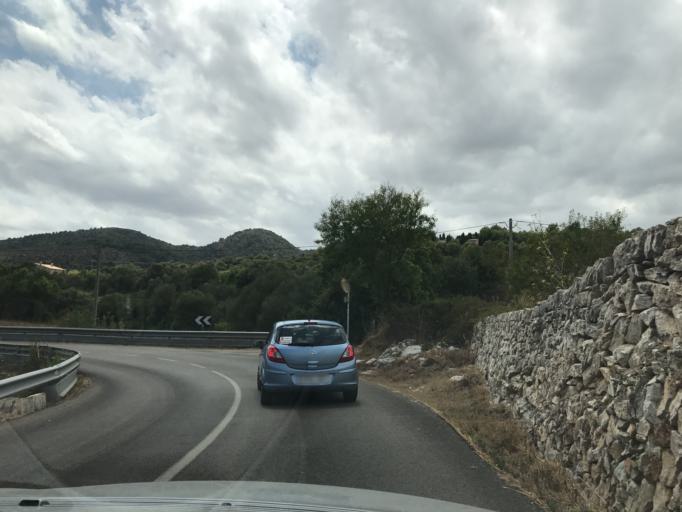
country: ES
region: Balearic Islands
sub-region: Illes Balears
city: Son Servera
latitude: 39.6470
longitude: 3.3458
